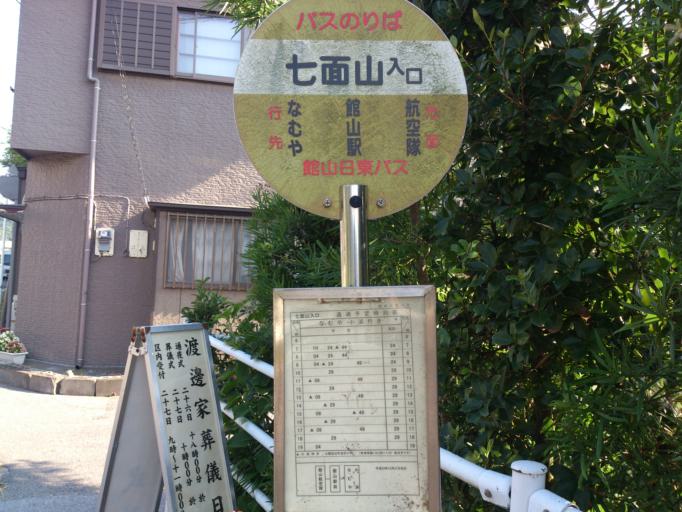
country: JP
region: Chiba
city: Tateyama
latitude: 35.0587
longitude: 139.8283
